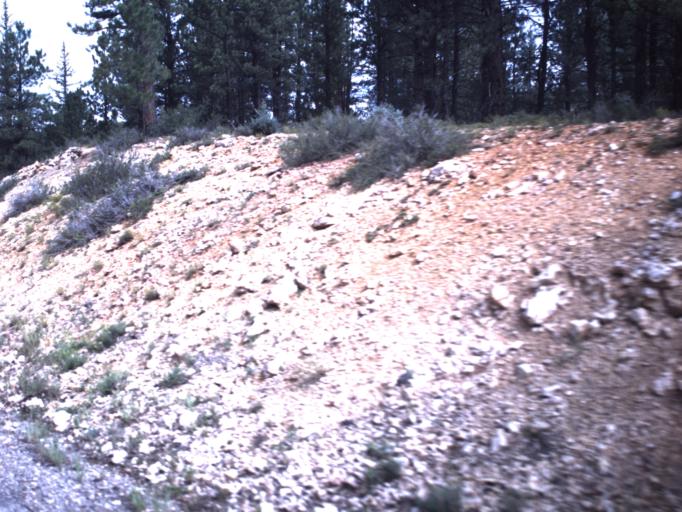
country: US
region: Utah
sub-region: Garfield County
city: Panguitch
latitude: 37.4983
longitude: -112.5891
